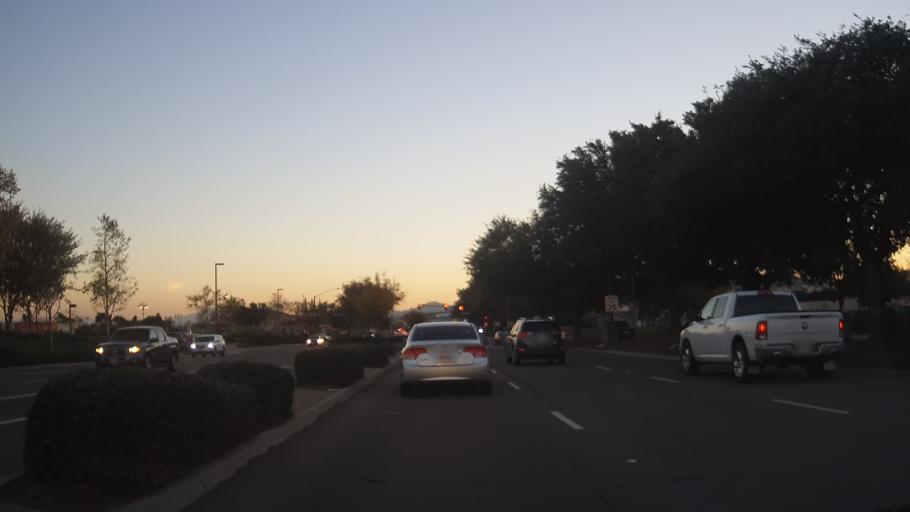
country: US
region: California
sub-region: San Diego County
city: Santee
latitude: 32.8427
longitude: -116.9839
